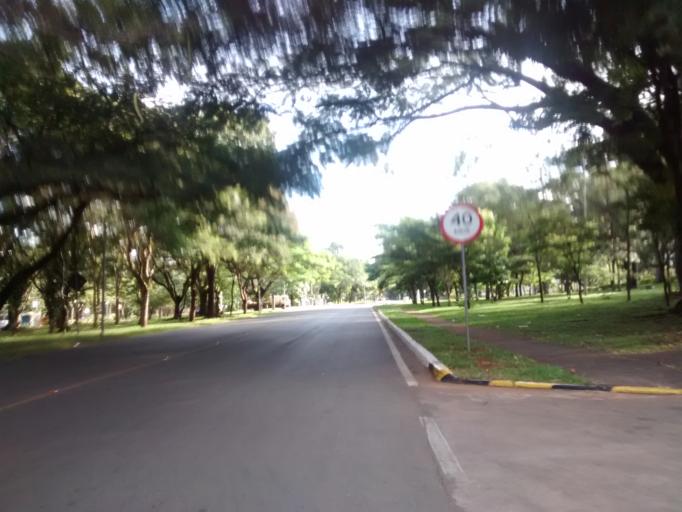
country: BR
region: Federal District
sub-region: Brasilia
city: Brasilia
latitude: -15.8092
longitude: -47.8970
